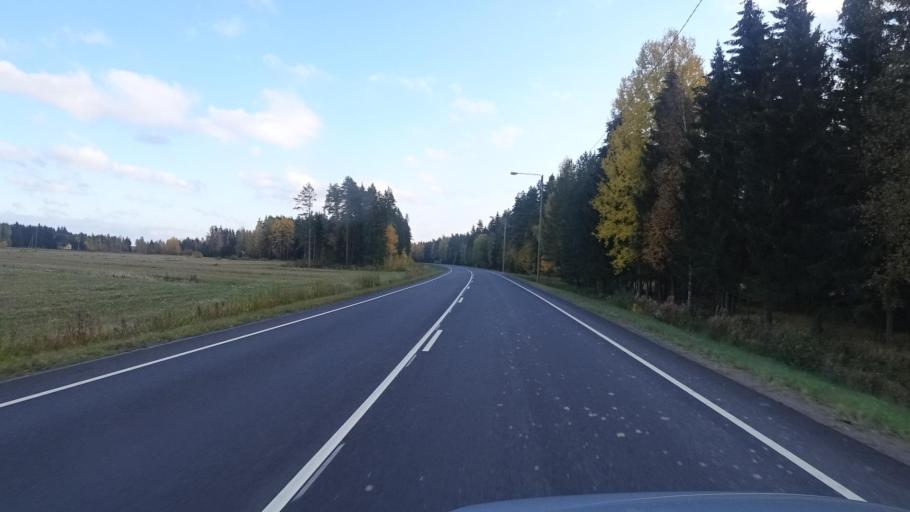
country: FI
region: Satakunta
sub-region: Rauma
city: Koeylioe
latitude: 61.0959
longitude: 22.2386
